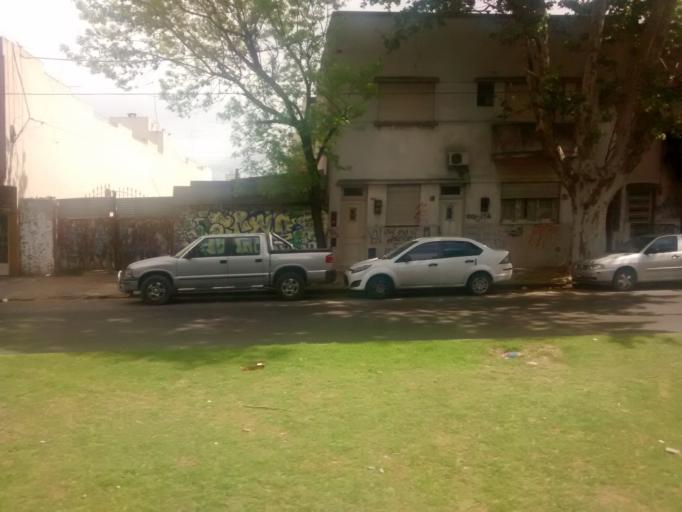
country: AR
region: Buenos Aires
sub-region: Partido de La Plata
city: La Plata
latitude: -34.9173
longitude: -57.9327
